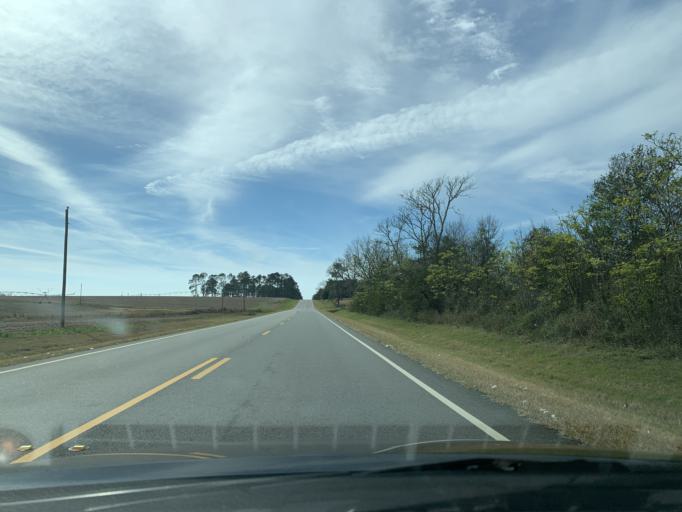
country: US
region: Georgia
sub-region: Turner County
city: Ashburn
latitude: 31.7844
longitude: -83.5102
